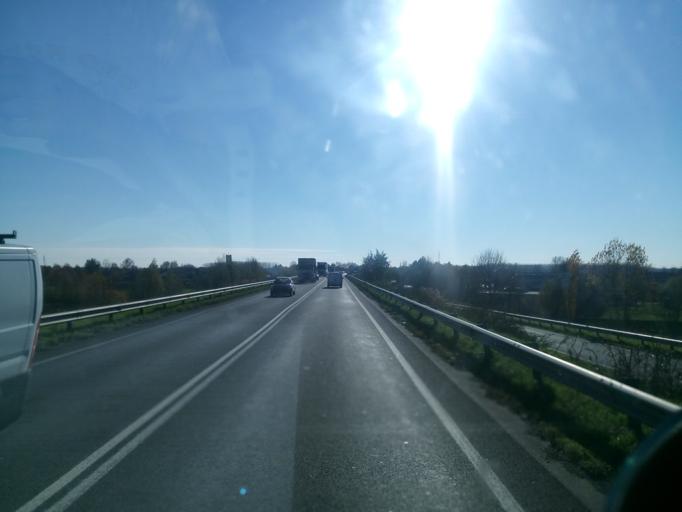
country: IT
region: Veneto
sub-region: Provincia di Padova
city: Mejaniga
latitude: 45.4690
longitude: 11.9199
